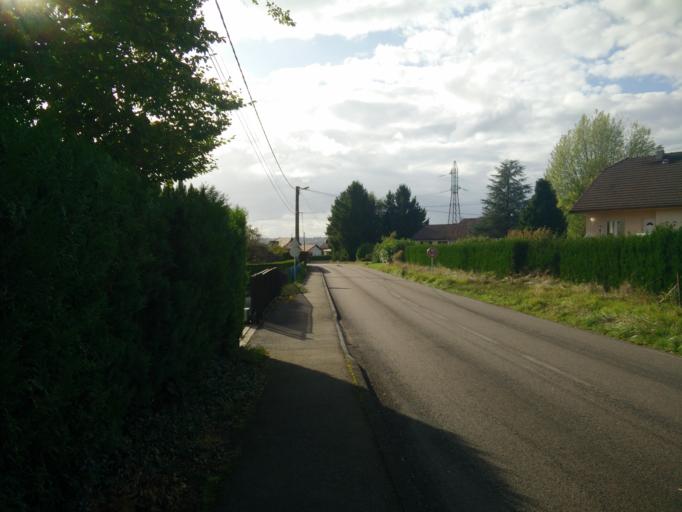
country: FR
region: Franche-Comte
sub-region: Departement du Doubs
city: Saone
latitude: 47.2268
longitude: 6.1262
